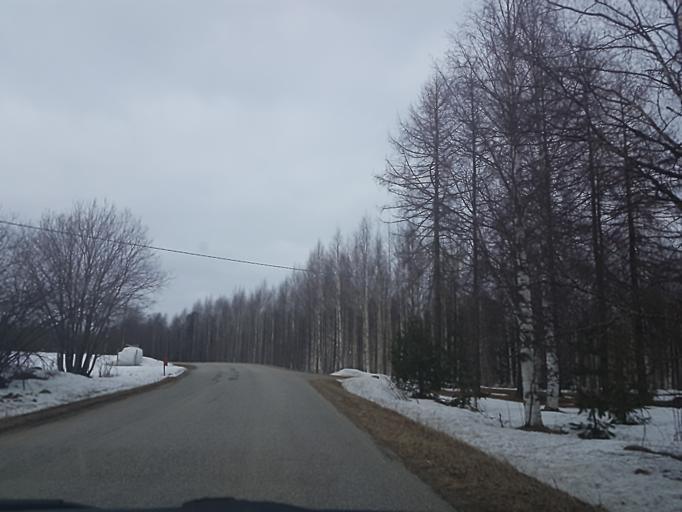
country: FI
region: Northern Savo
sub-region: Koillis-Savo
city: Kaavi
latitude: 62.9923
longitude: 28.7228
